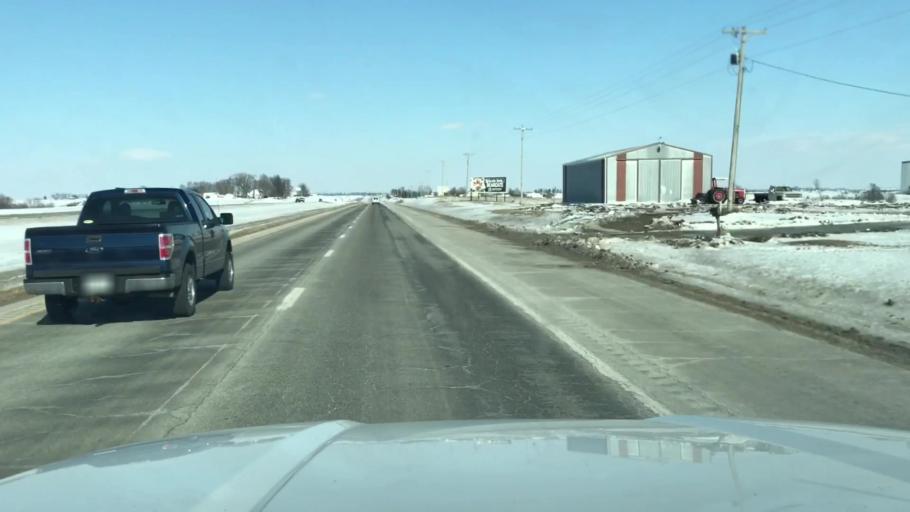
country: US
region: Missouri
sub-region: Nodaway County
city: Maryville
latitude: 40.2834
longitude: -94.8754
